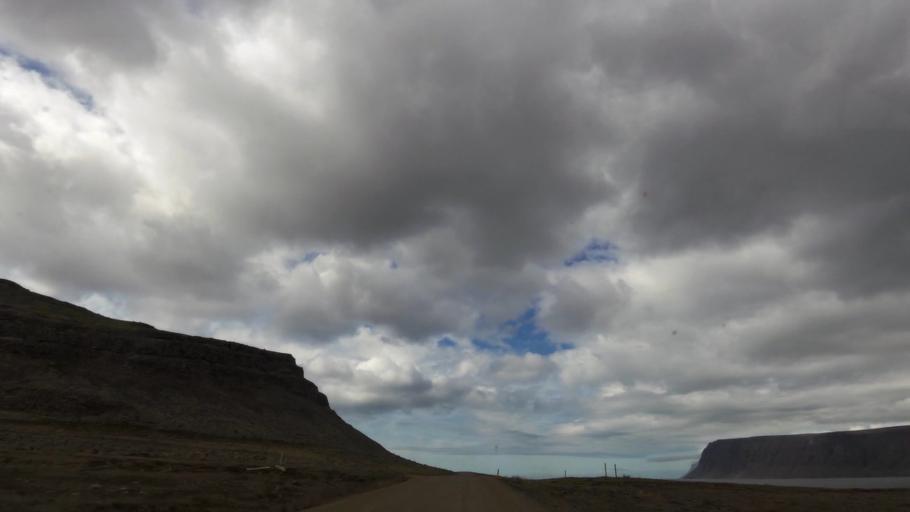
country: IS
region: West
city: Olafsvik
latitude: 65.5717
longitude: -24.0620
